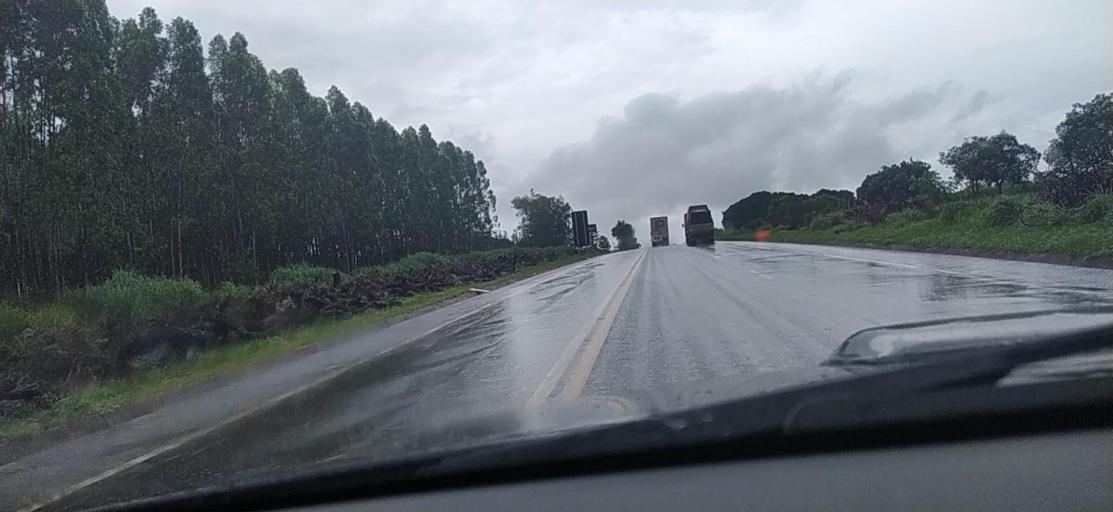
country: BR
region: Minas Gerais
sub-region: Curvelo
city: Curvelo
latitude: -18.9426
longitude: -44.4973
